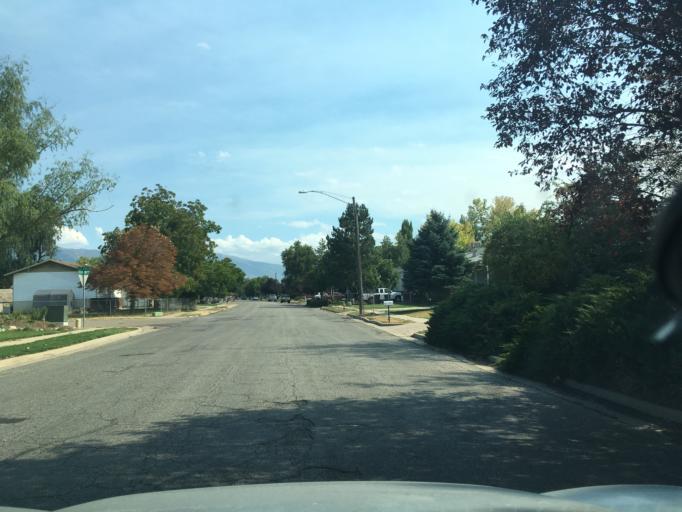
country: US
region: Utah
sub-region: Davis County
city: Clearfield
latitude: 41.0827
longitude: -112.0034
